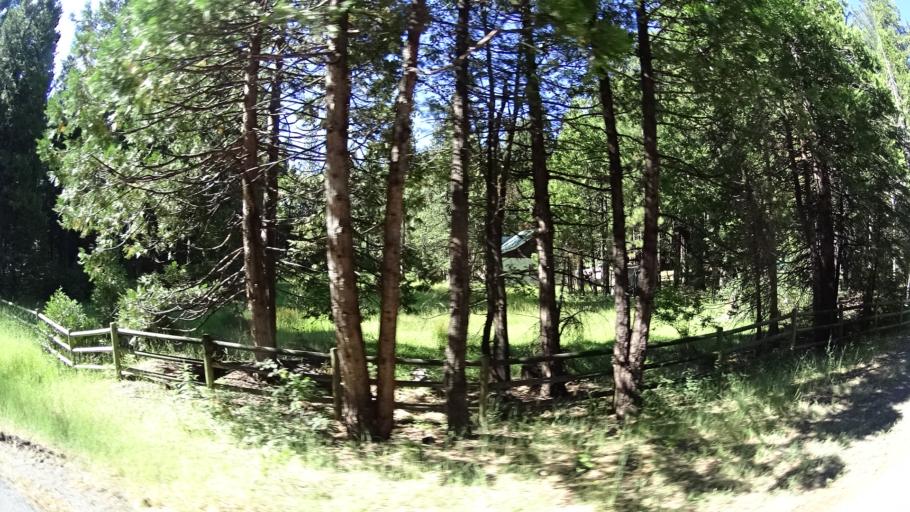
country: US
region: California
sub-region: Calaveras County
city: Arnold
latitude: 38.3001
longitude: -120.2670
